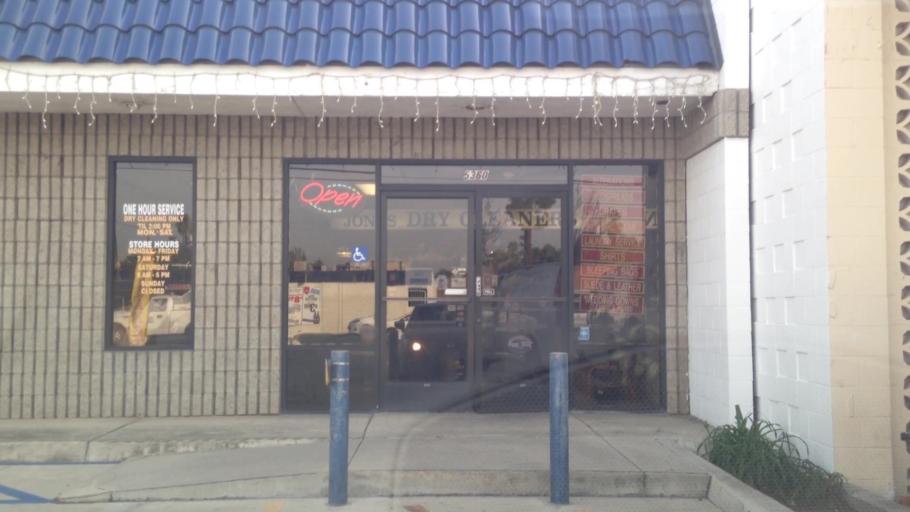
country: US
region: California
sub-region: Riverside County
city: Riverside
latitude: 33.9458
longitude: -117.4198
